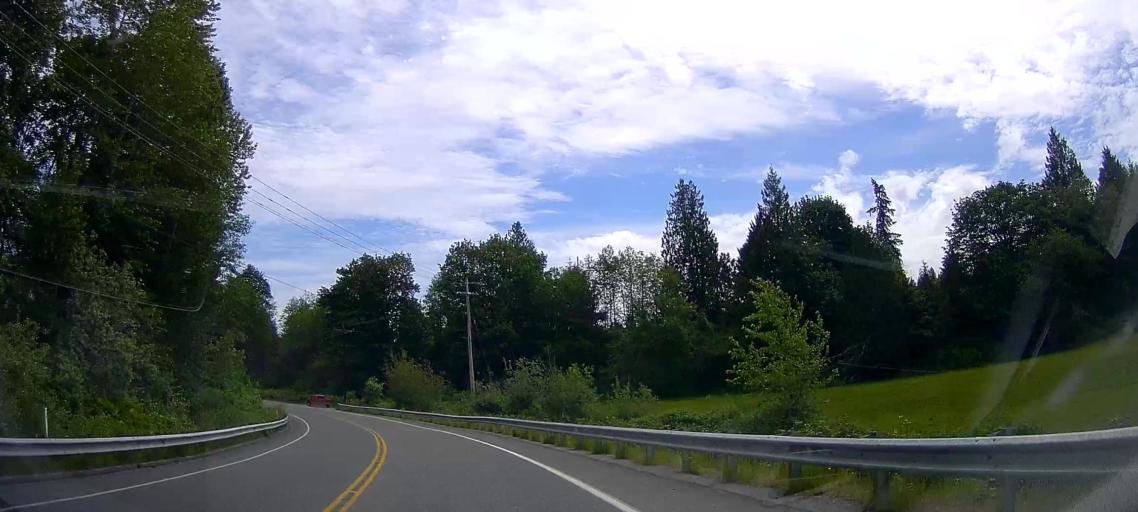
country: US
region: Washington
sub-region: Snohomish County
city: Bryant
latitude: 48.2385
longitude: -122.2036
